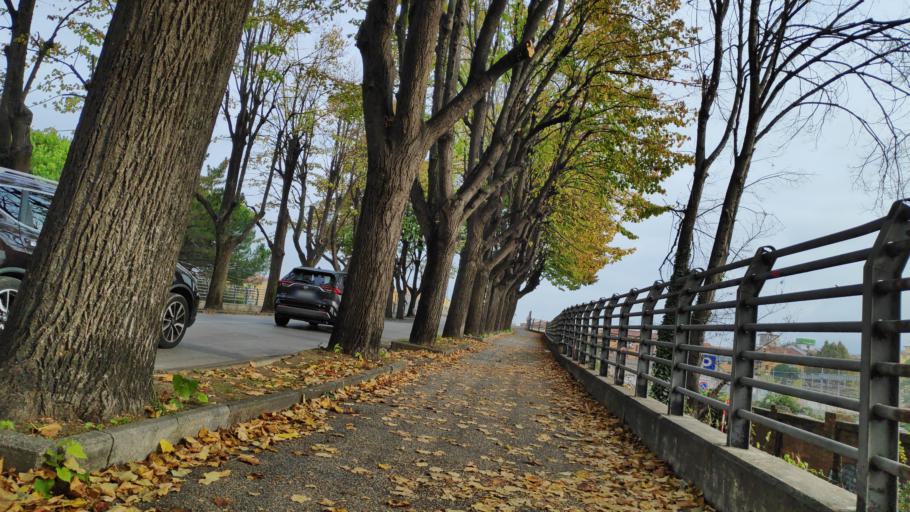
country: IT
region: Tuscany
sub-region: Province of Pisa
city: Pisa
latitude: 43.7056
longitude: 10.4023
